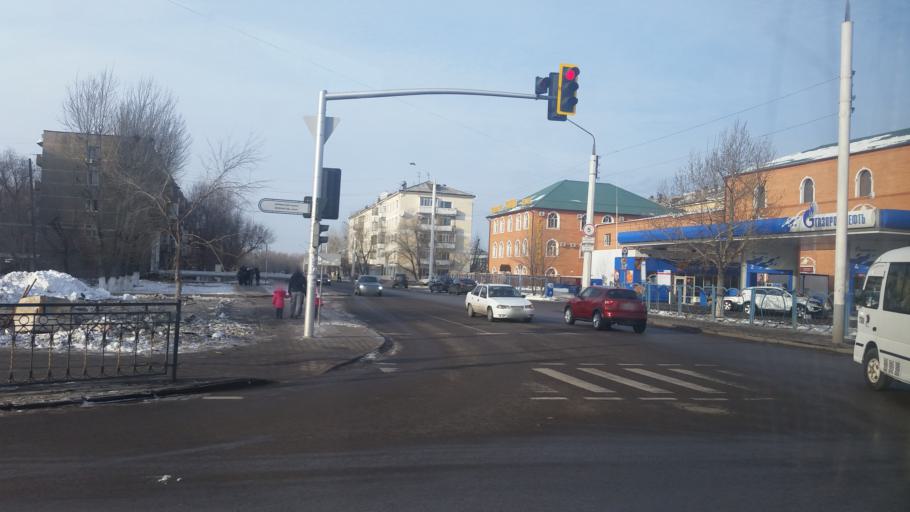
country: KZ
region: Astana Qalasy
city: Astana
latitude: 51.1934
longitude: 71.4079
